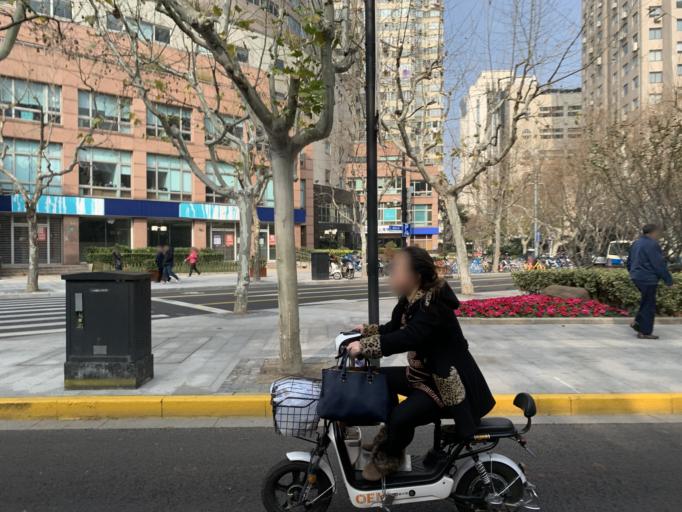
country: CN
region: Shanghai Shi
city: Xuhui
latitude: 31.2001
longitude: 121.4414
